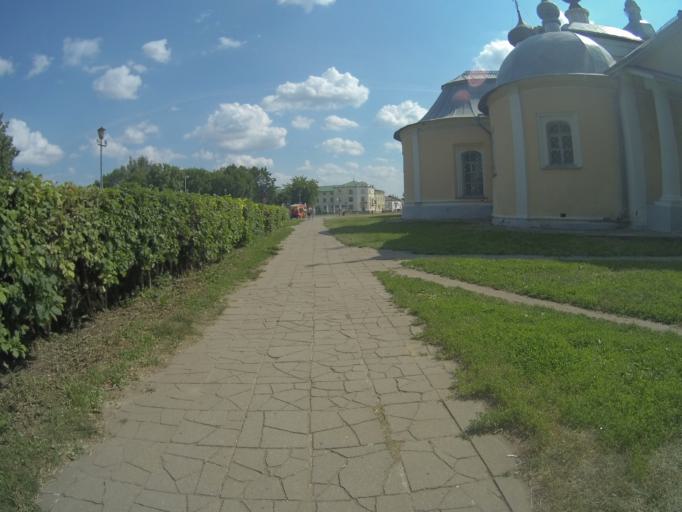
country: RU
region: Vladimir
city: Suzdal'
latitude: 56.4202
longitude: 40.4491
